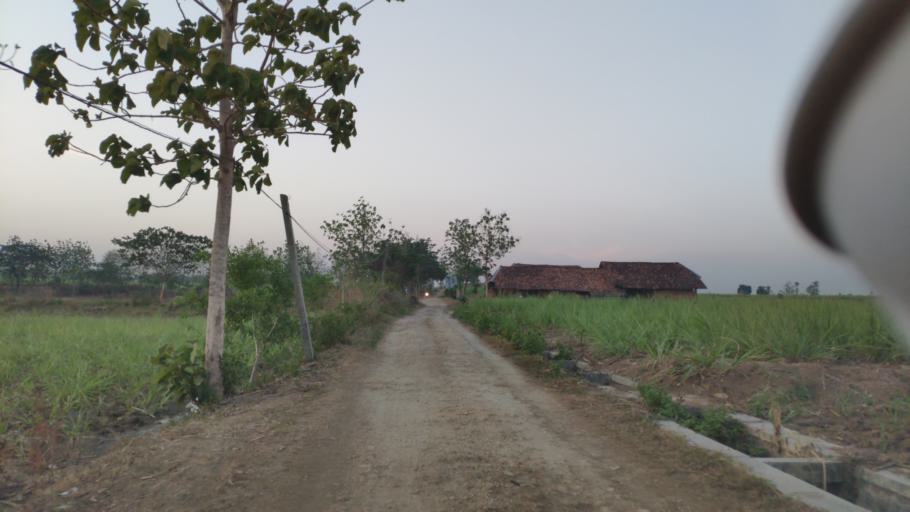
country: ID
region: Central Java
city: Jepang
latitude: -7.0322
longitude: 111.2387
